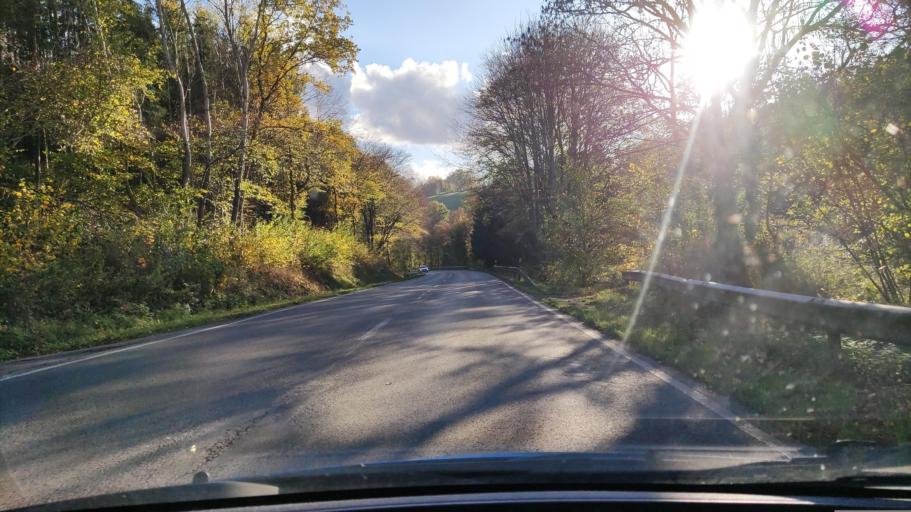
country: DE
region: Lower Saxony
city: Heinade
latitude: 51.8323
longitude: 9.6353
